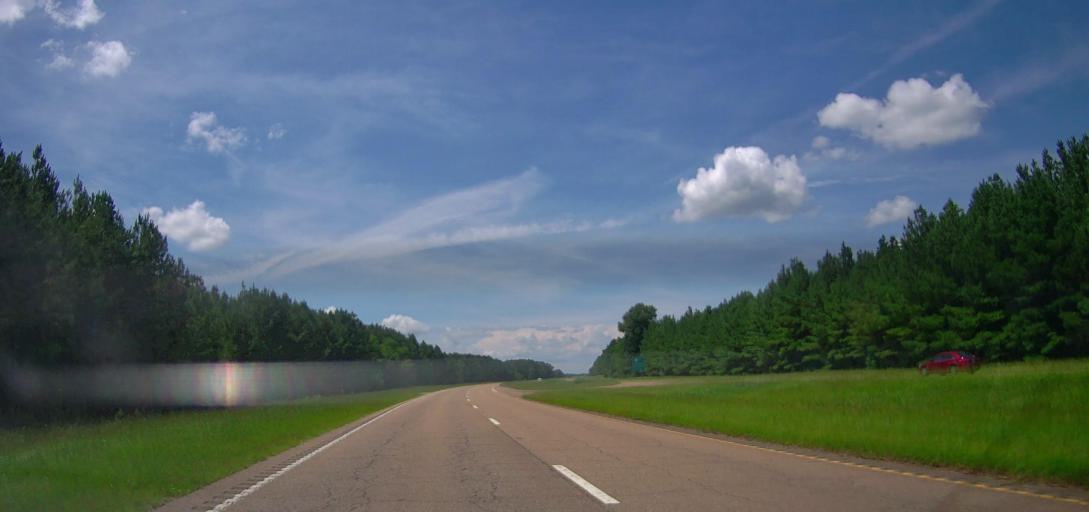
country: US
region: Mississippi
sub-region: Monroe County
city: Aberdeen
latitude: 33.8202
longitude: -88.5817
